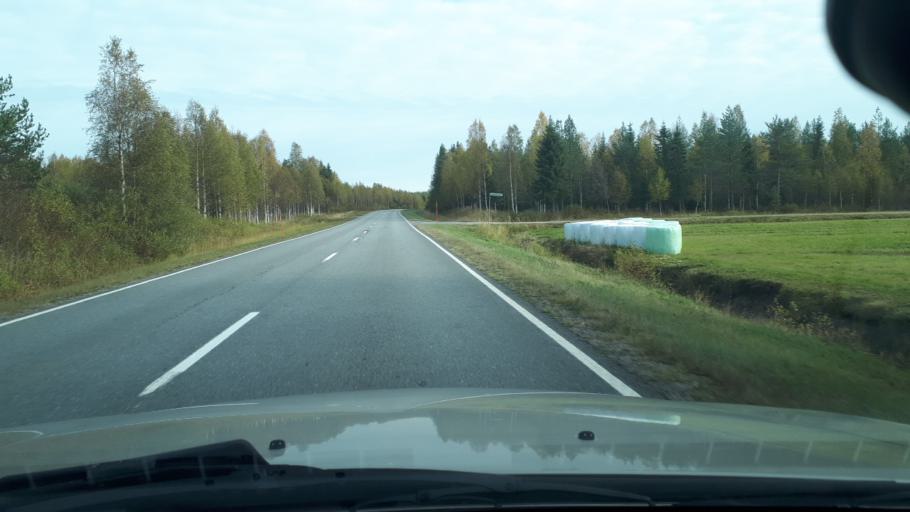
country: FI
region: Lapland
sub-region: Rovaniemi
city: Ranua
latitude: 65.9765
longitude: 26.1191
